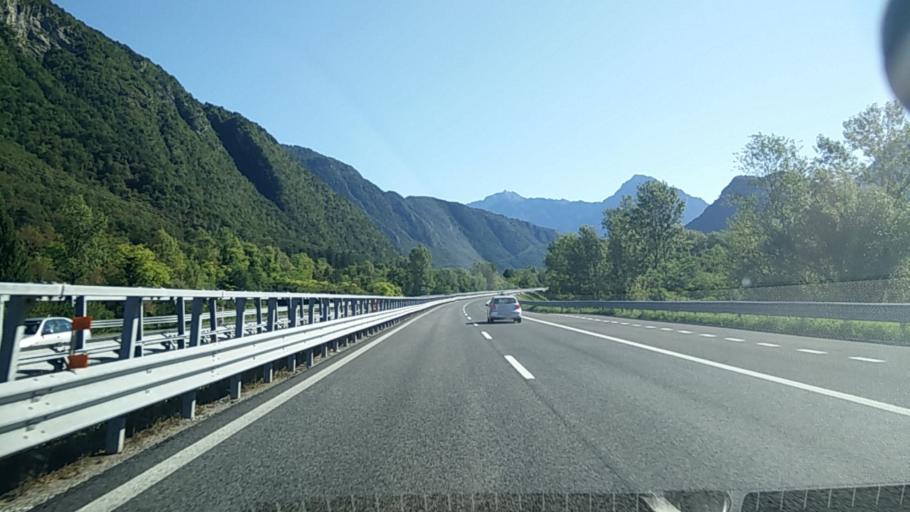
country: IT
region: Friuli Venezia Giulia
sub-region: Provincia di Udine
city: Amaro
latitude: 46.3742
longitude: 13.1054
